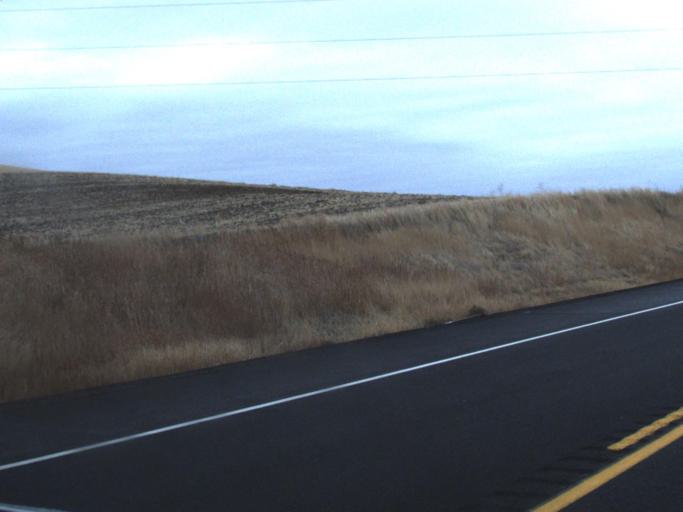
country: US
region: Washington
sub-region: Whitman County
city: Pullman
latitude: 46.7755
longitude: -117.2823
